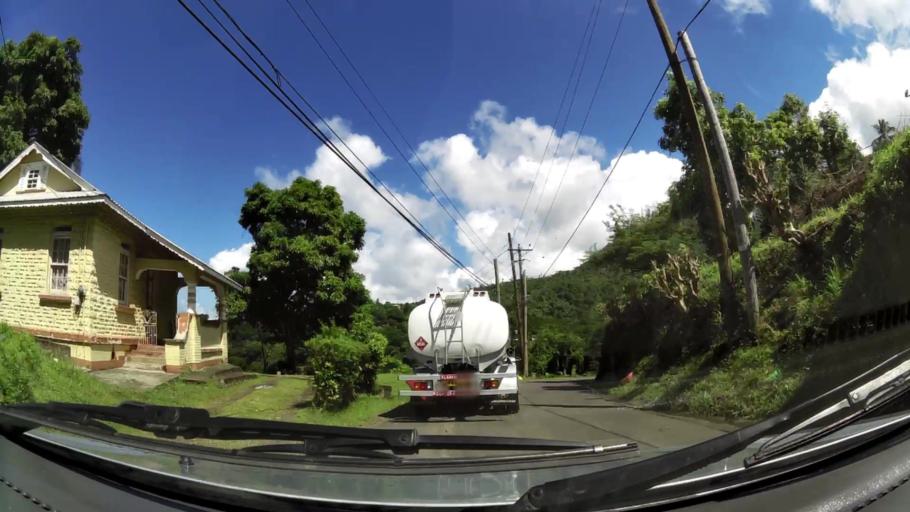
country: GD
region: Saint John
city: Gouyave
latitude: 12.1166
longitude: -61.7440
